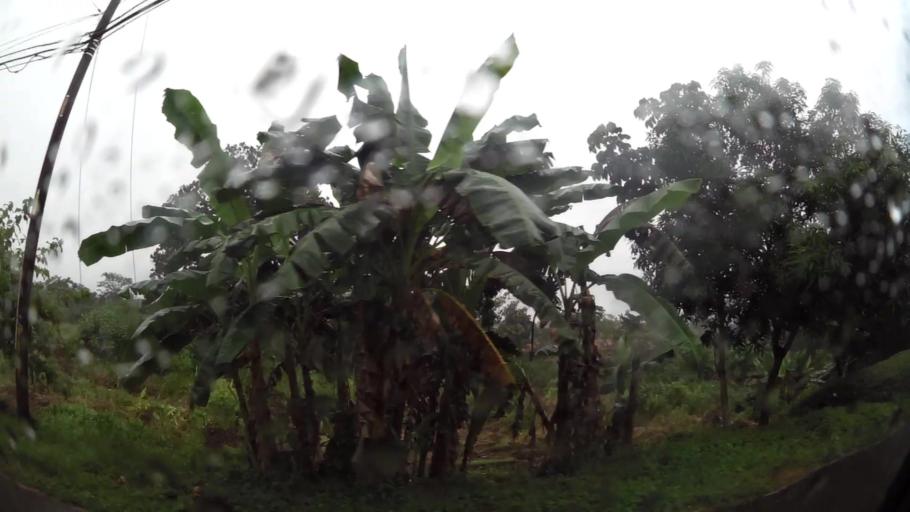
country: PA
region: Panama
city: Cabra Numero Uno
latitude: 9.1033
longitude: -79.3359
